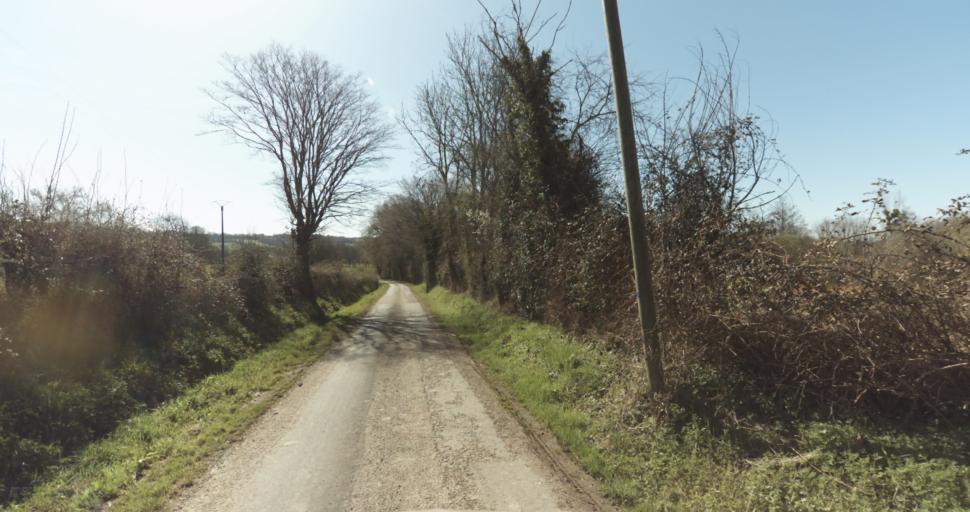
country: FR
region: Lower Normandy
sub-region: Departement du Calvados
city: Livarot
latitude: 48.9618
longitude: 0.0678
